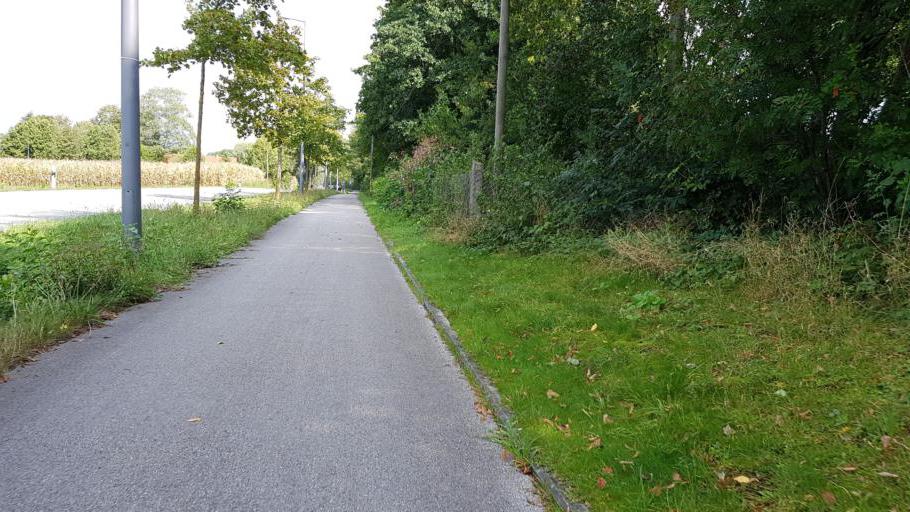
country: DE
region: Bavaria
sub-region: Upper Bavaria
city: Karlsfeld
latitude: 48.2165
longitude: 11.5096
